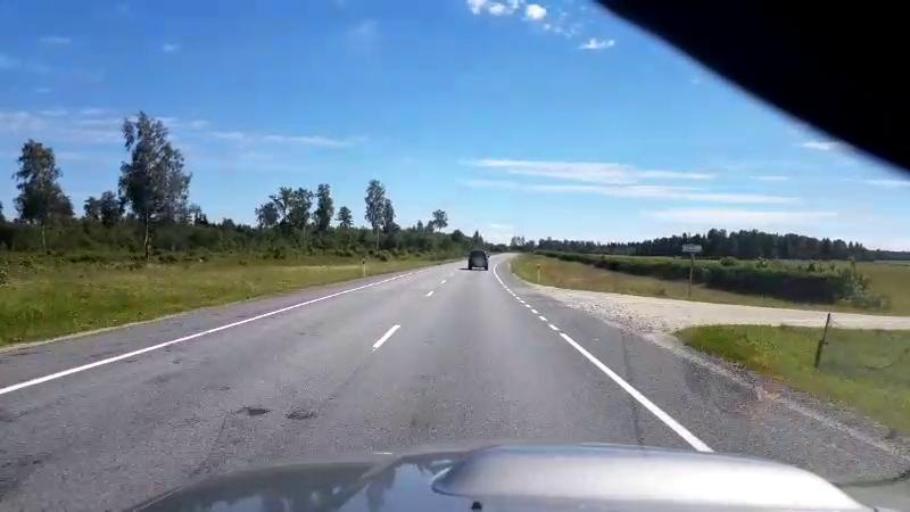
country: EE
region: Jaervamaa
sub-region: Jaerva-Jaani vald
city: Jarva-Jaani
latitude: 59.0227
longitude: 25.8994
